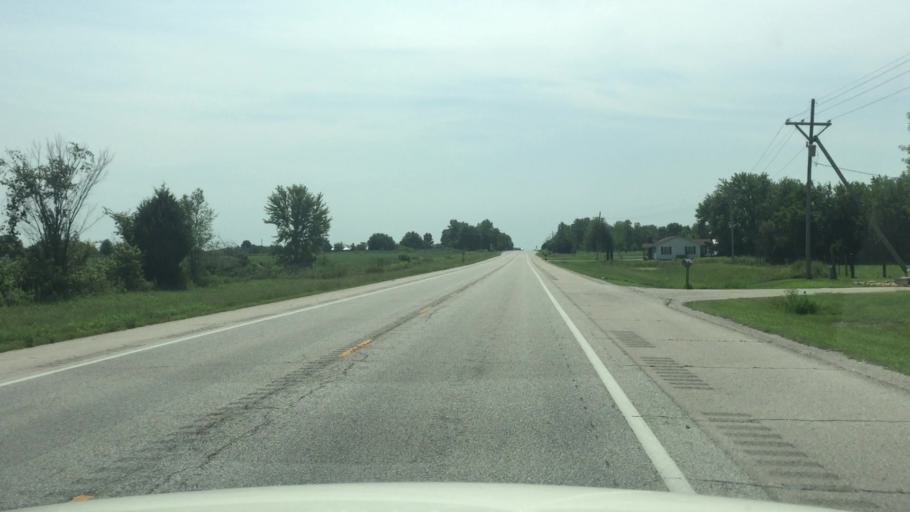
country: US
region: Kansas
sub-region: Cherokee County
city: Galena
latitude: 37.1091
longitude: -94.7044
